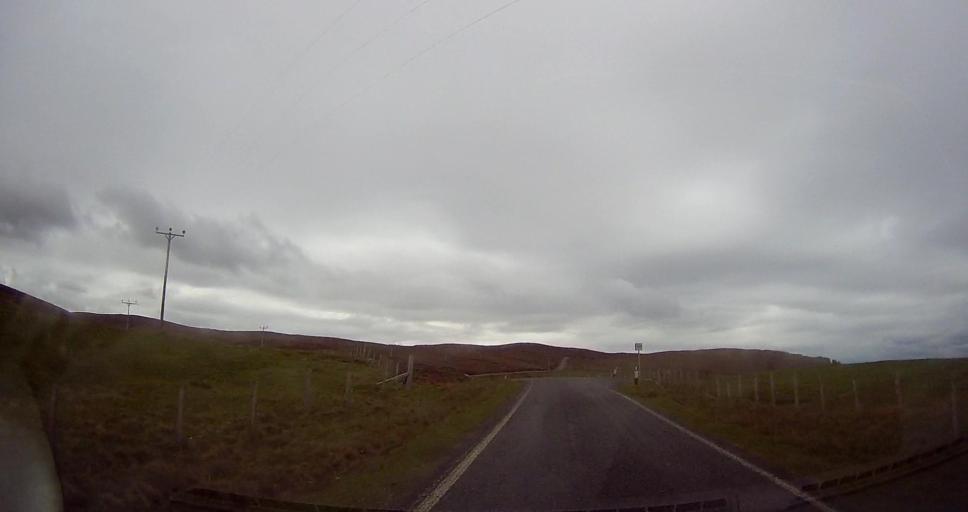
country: GB
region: Scotland
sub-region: Shetland Islands
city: Lerwick
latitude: 60.4928
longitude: -1.5499
